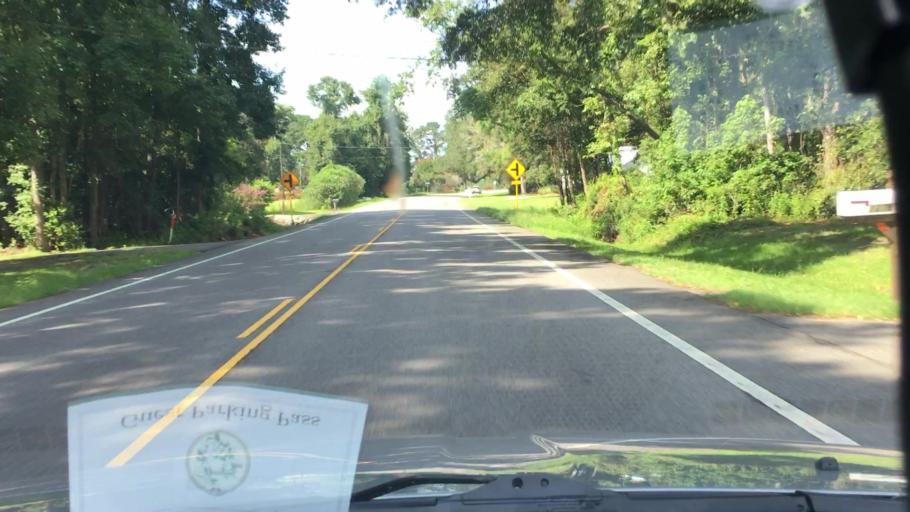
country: US
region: South Carolina
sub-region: Beaufort County
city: Beaufort
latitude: 32.4015
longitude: -80.5370
